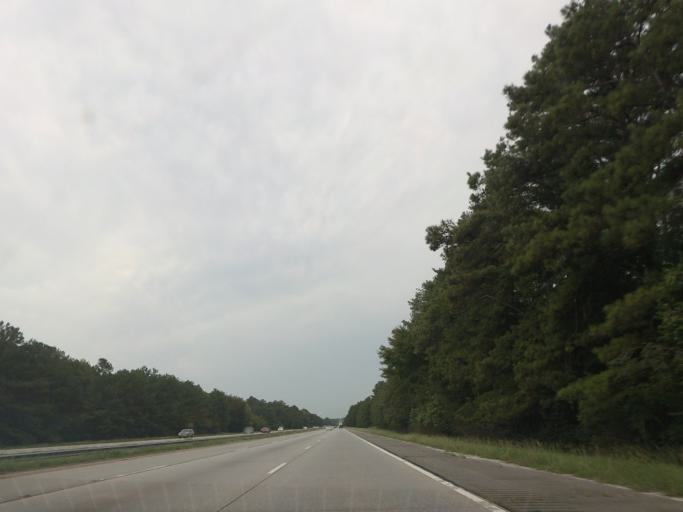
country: US
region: Georgia
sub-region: Bibb County
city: Macon
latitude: 32.7735
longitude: -83.6908
